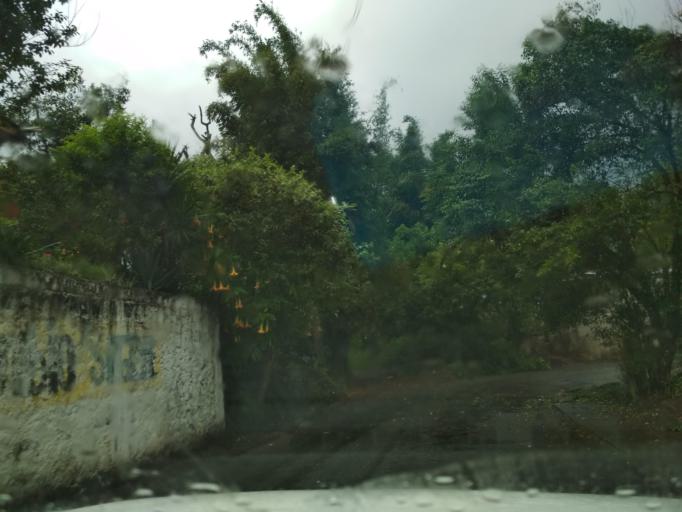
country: MX
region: Veracruz
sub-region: Mariano Escobedo
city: Chicola
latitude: 18.9029
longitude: -97.1178
